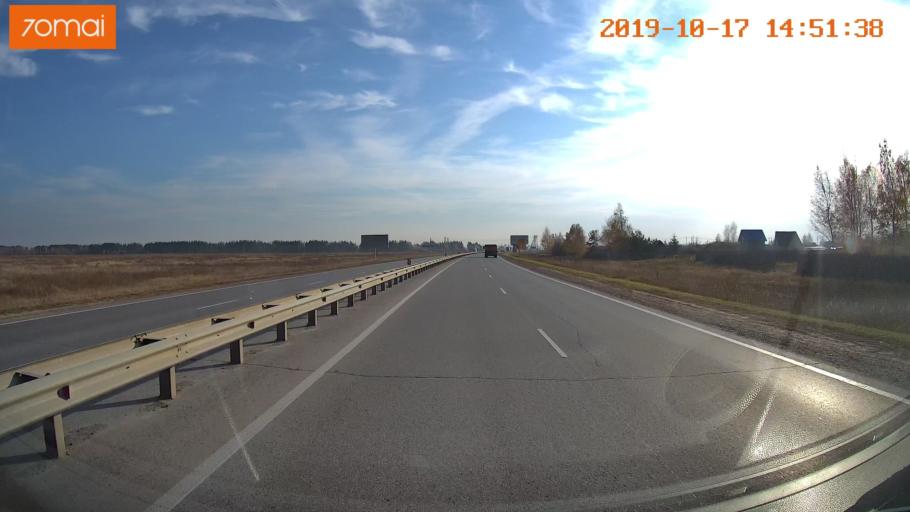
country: RU
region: Rjazan
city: Polyany
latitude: 54.7168
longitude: 39.8485
